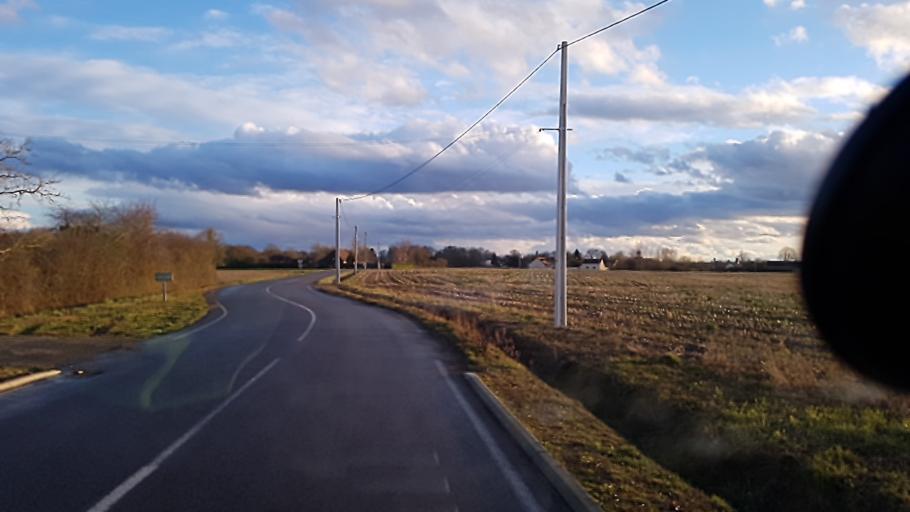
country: FR
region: Bourgogne
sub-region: Departement de Saone-et-Loire
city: Saint-Martin-en-Bresse
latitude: 46.7419
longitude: 5.0806
